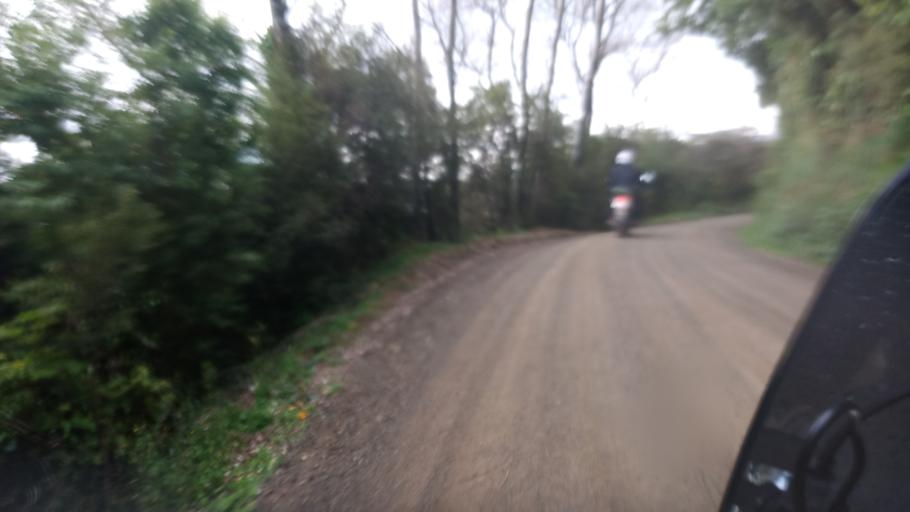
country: NZ
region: Gisborne
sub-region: Gisborne District
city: Gisborne
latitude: -38.4747
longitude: 177.6152
